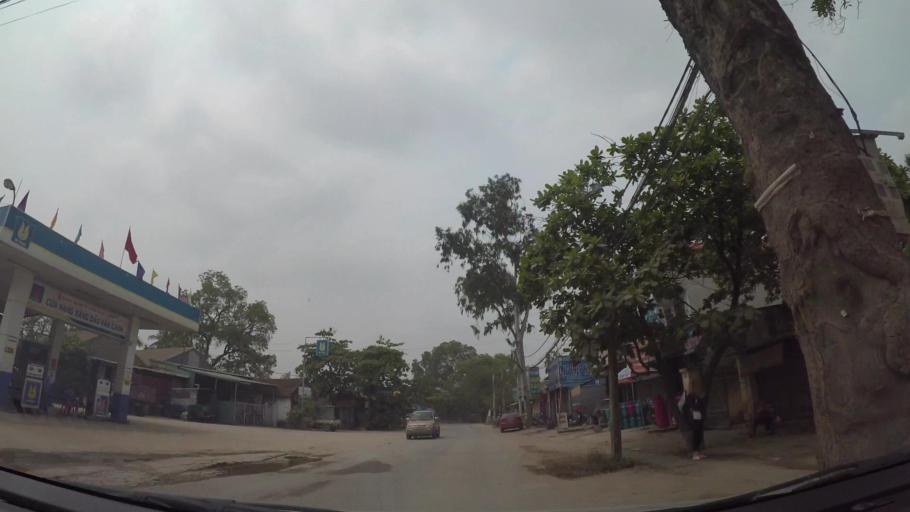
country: VN
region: Ha Noi
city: Cau Dien
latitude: 21.0359
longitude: 105.7383
